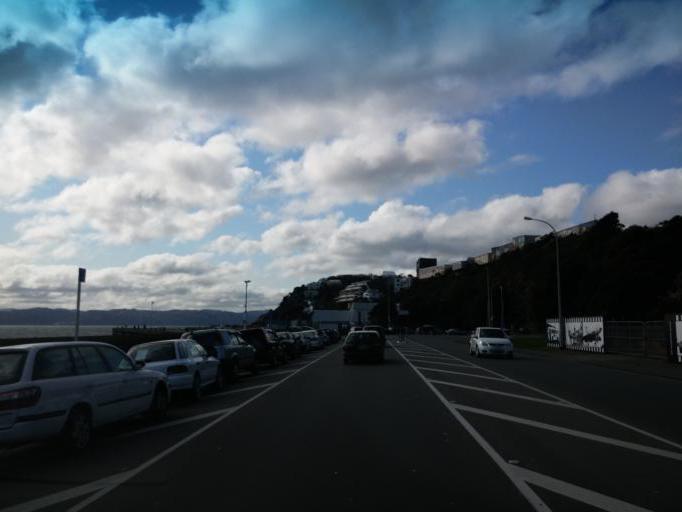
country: NZ
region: Wellington
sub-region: Wellington City
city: Wellington
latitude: -41.3153
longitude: 174.8104
